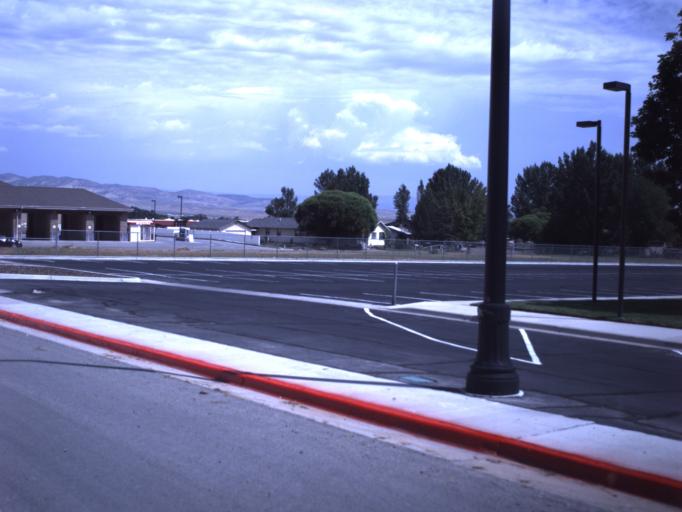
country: US
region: Utah
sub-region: Uintah County
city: Naples
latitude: 40.4223
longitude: -109.4993
